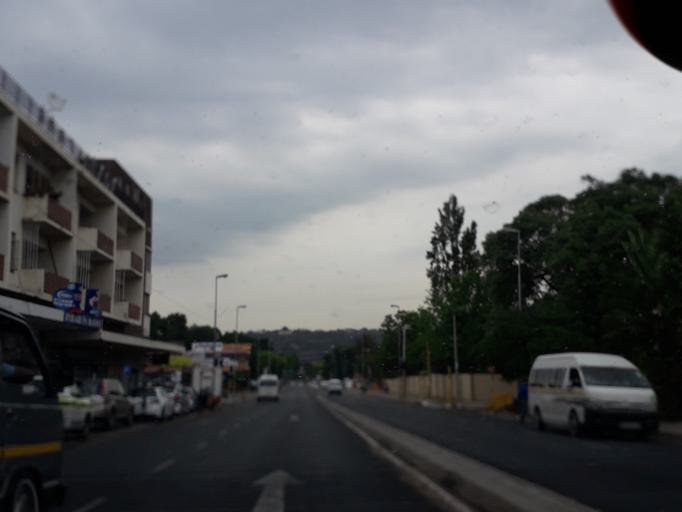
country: ZA
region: Gauteng
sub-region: City of Johannesburg Metropolitan Municipality
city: Johannesburg
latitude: -26.1477
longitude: 28.0867
